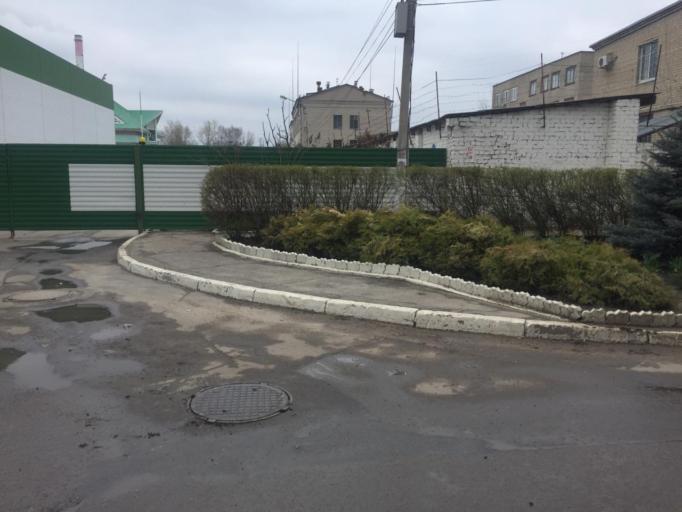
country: RU
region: Voronezj
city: Voronezh
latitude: 51.6793
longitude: 39.1549
